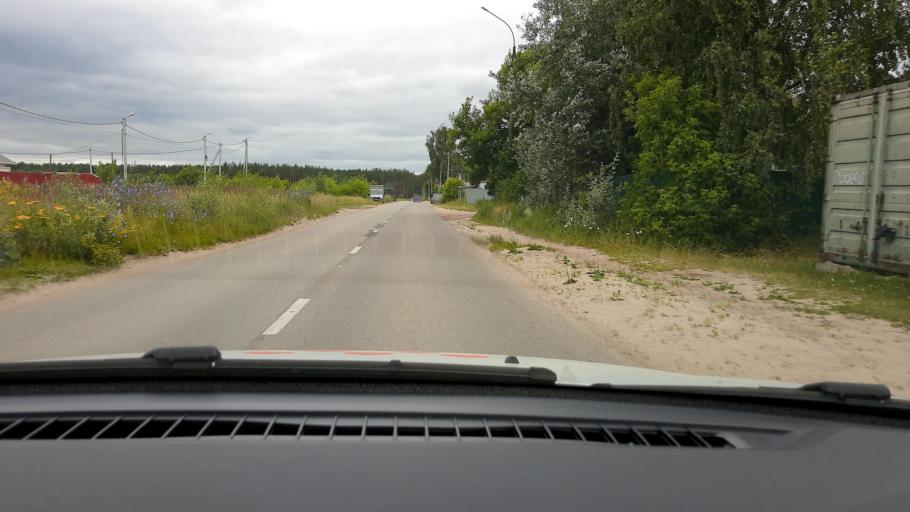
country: RU
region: Nizjnij Novgorod
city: Pyra
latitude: 56.2404
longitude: 43.3811
